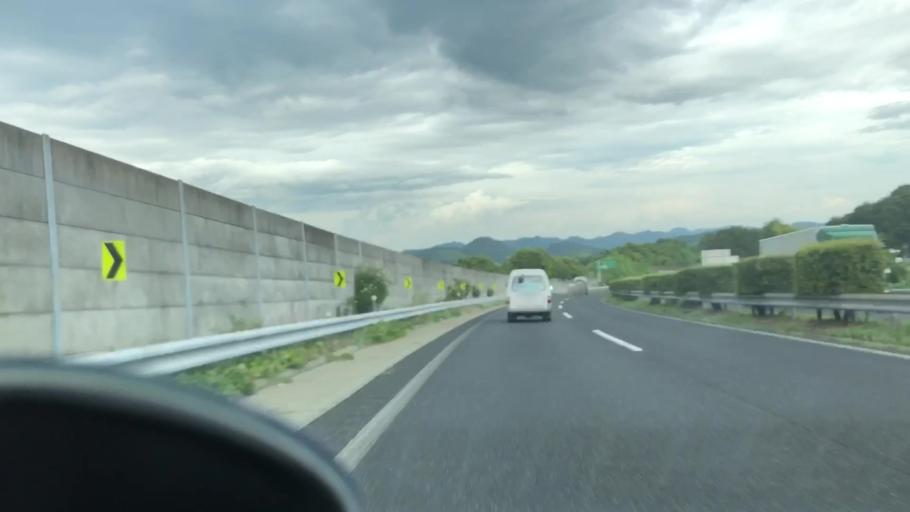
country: JP
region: Hyogo
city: Yashiro
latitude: 34.9358
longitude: 134.8507
